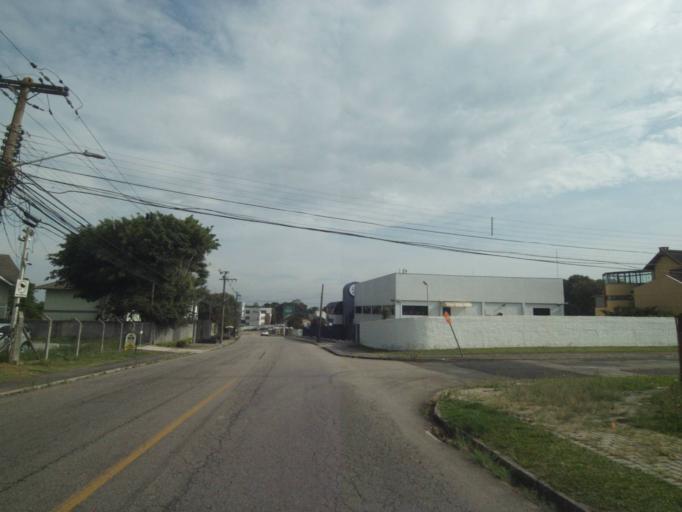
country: BR
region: Parana
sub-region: Curitiba
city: Curitiba
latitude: -25.4088
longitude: -49.3126
